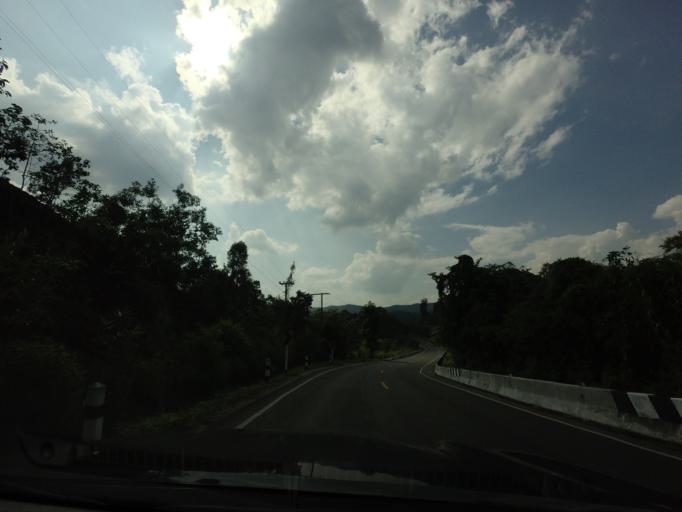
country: TH
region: Uttaradit
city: Ban Khok
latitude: 18.2096
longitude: 101.0455
